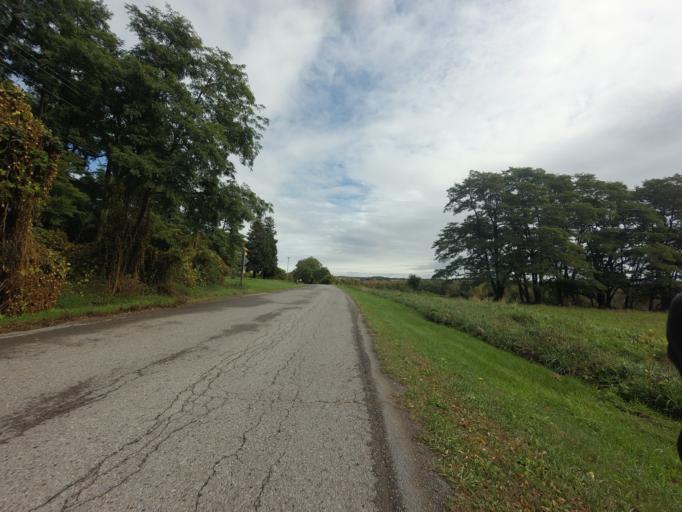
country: CA
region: Ontario
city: Cobourg
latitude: 43.9303
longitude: -78.3828
